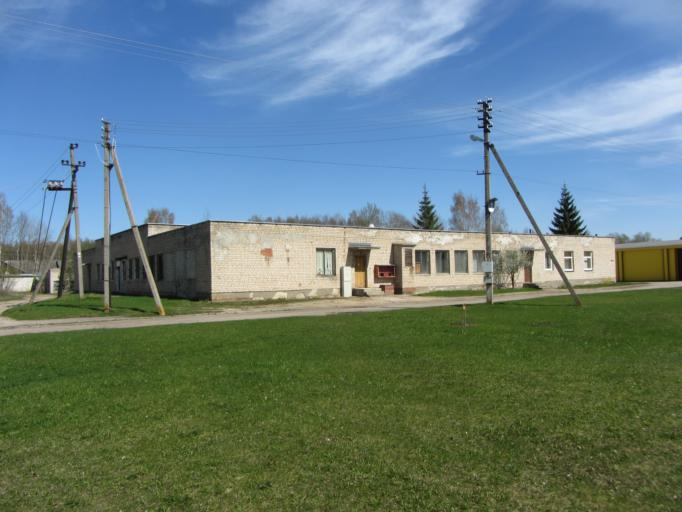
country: LT
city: Zarasai
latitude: 55.7435
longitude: 26.2717
